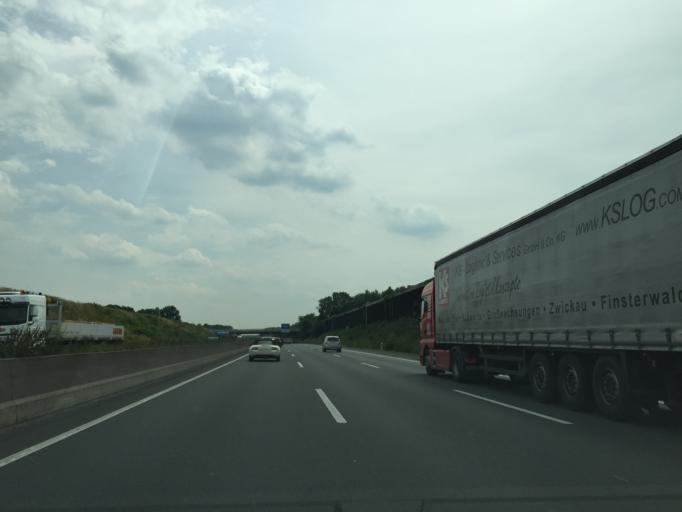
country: DE
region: North Rhine-Westphalia
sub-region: Regierungsbezirk Munster
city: Muenster
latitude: 51.9568
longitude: 7.5463
